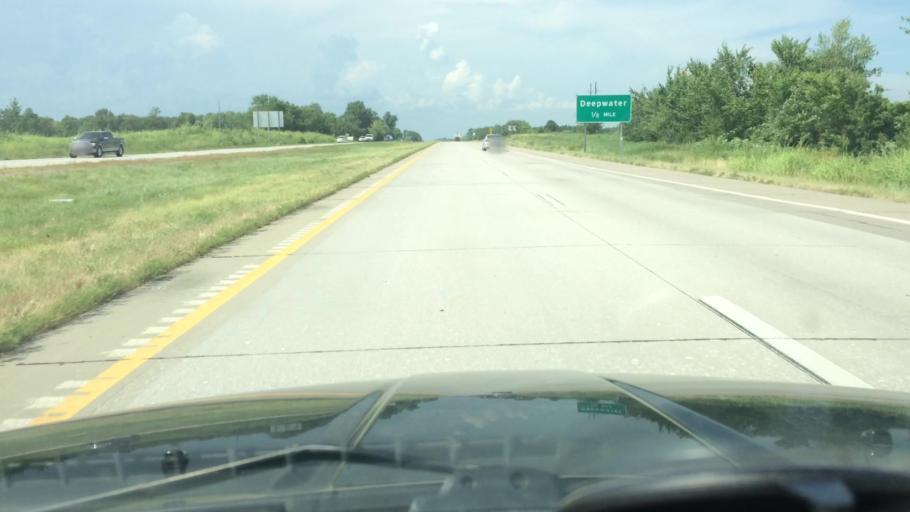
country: US
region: Missouri
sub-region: Henry County
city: Clinton
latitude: 38.2553
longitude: -93.7608
